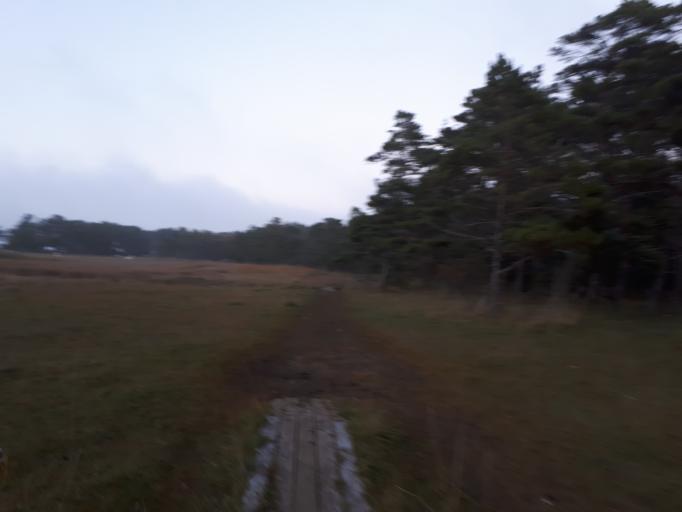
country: SE
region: Gotland
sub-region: Gotland
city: Visby
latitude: 57.6853
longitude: 18.3458
